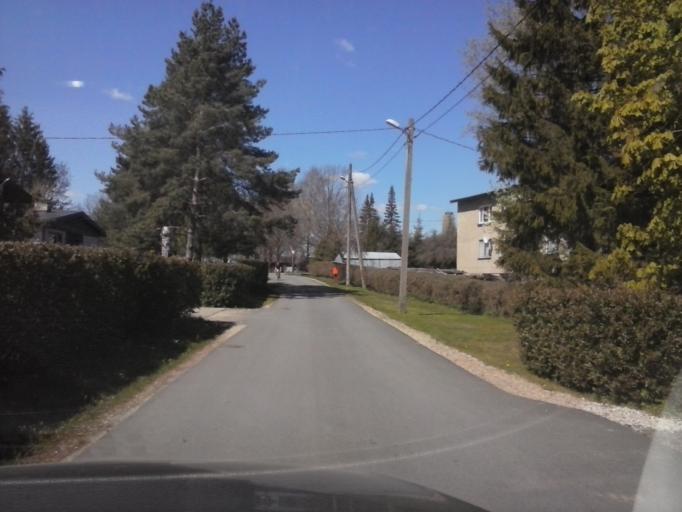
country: EE
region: Valgamaa
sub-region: Torva linn
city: Torva
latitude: 58.1491
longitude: 25.9768
